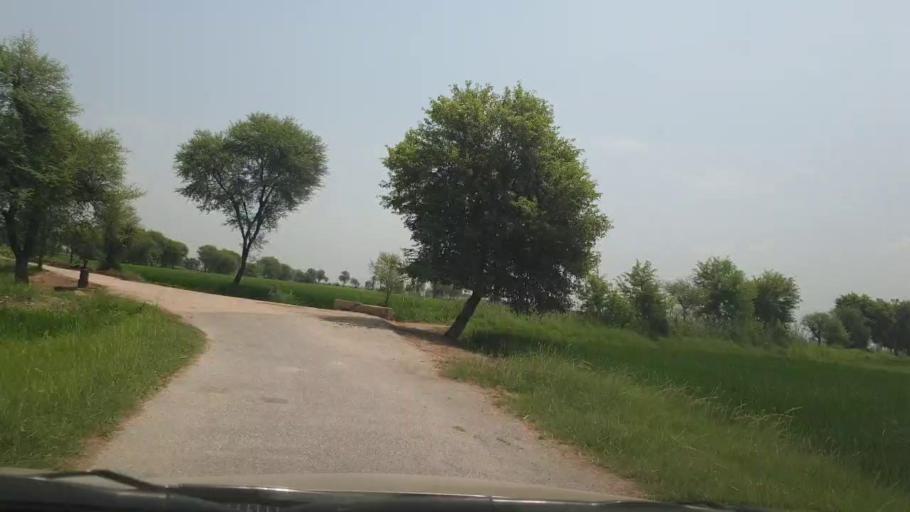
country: PK
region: Sindh
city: Ratodero
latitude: 27.7352
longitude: 68.3025
